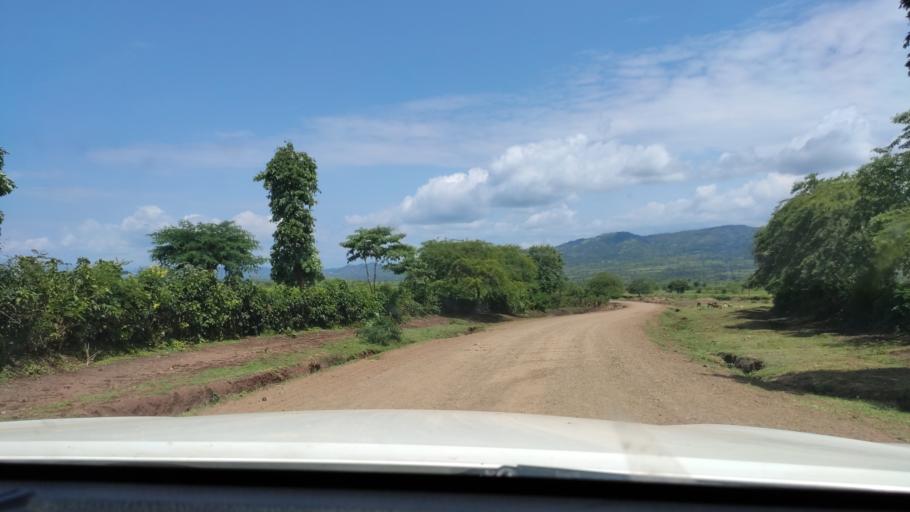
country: ET
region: Southern Nations, Nationalities, and People's Region
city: Felege Neway
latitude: 6.3653
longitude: 36.9880
